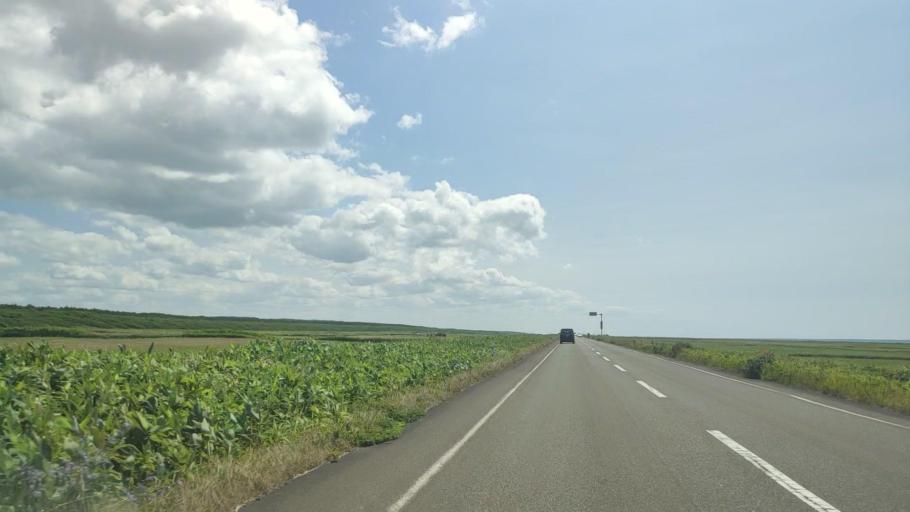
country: JP
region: Hokkaido
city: Wakkanai
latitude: 45.1414
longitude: 141.5997
